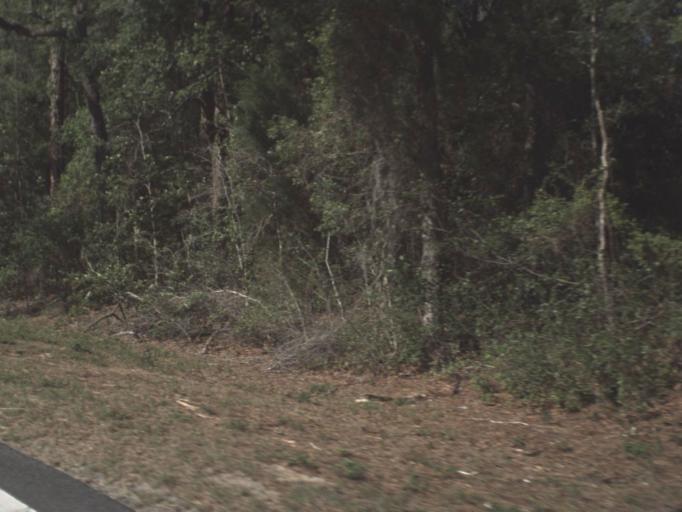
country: US
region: Florida
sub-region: Marion County
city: Dunnellon
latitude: 29.1986
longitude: -82.4372
